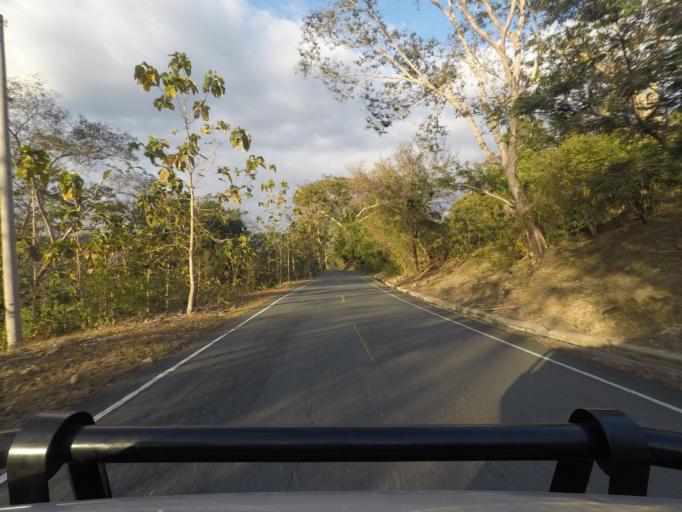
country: TL
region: Bobonaro
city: Maliana
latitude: -8.9474
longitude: 125.0965
